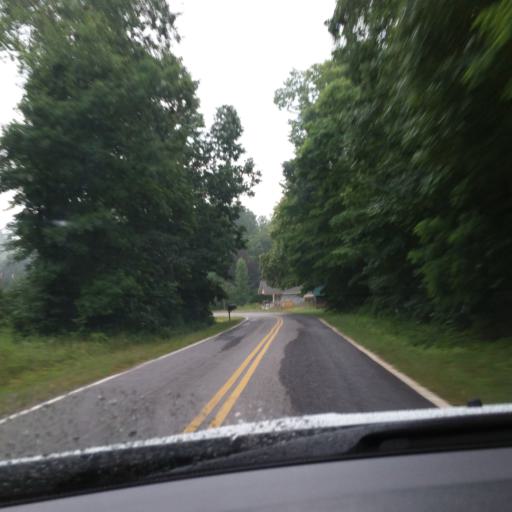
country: US
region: North Carolina
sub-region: Yancey County
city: Burnsville
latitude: 35.8306
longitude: -82.2000
